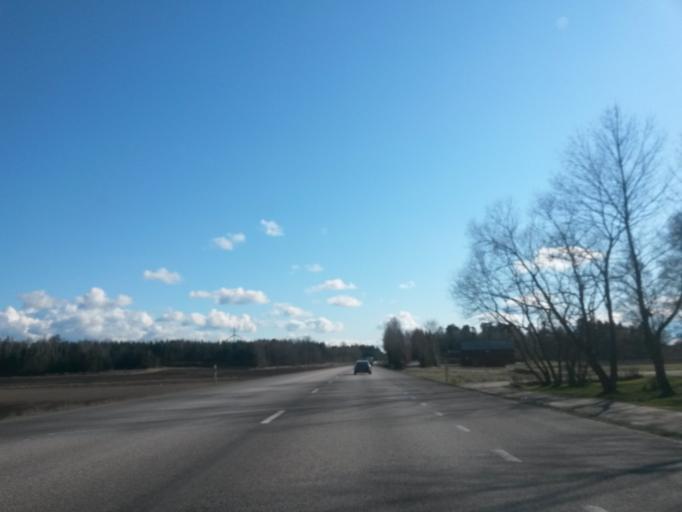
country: SE
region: Vaestra Goetaland
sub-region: Vargarda Kommun
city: Vargarda
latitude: 58.1333
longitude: 12.8591
